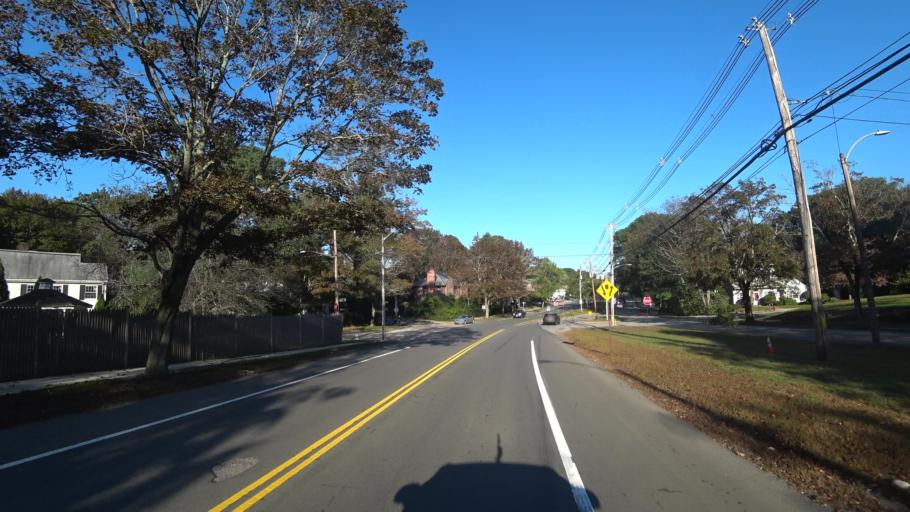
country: US
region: Massachusetts
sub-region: Middlesex County
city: Newton
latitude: 42.3398
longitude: -71.2366
